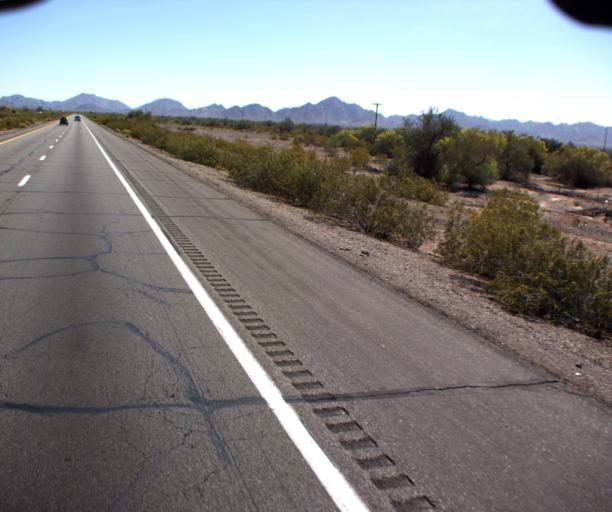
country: US
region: Arizona
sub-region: La Paz County
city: Quartzsite
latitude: 33.6675
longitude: -114.1806
